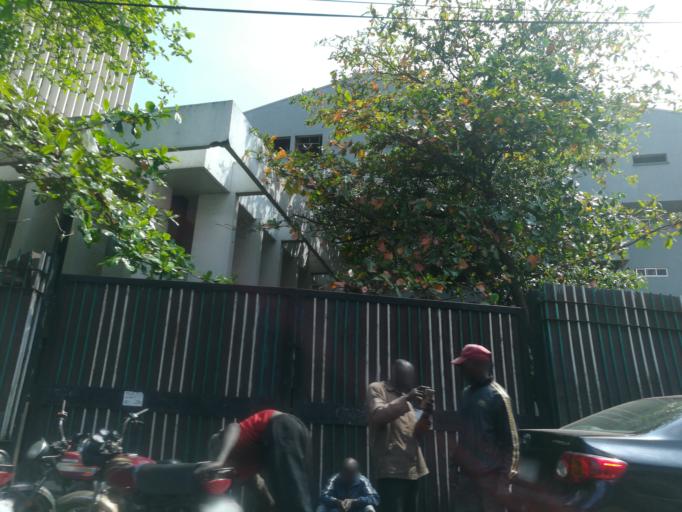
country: NG
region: Lagos
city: Lagos
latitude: 6.4494
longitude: 3.3982
